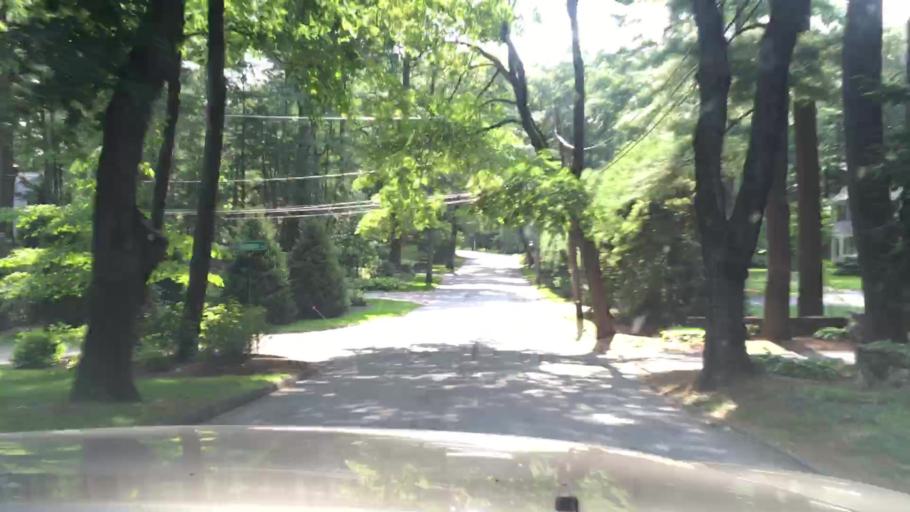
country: US
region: Massachusetts
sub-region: Norfolk County
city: Wellesley
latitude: 42.3153
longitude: -71.2840
